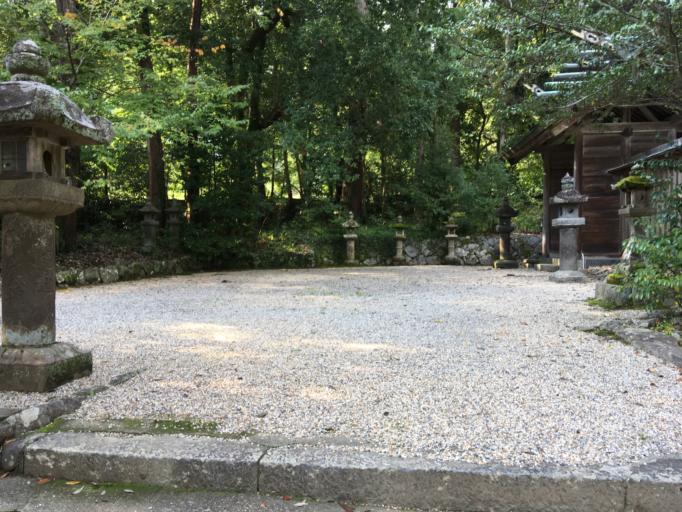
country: JP
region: Nara
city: Haibara-akanedai
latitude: 34.4784
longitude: 135.9239
